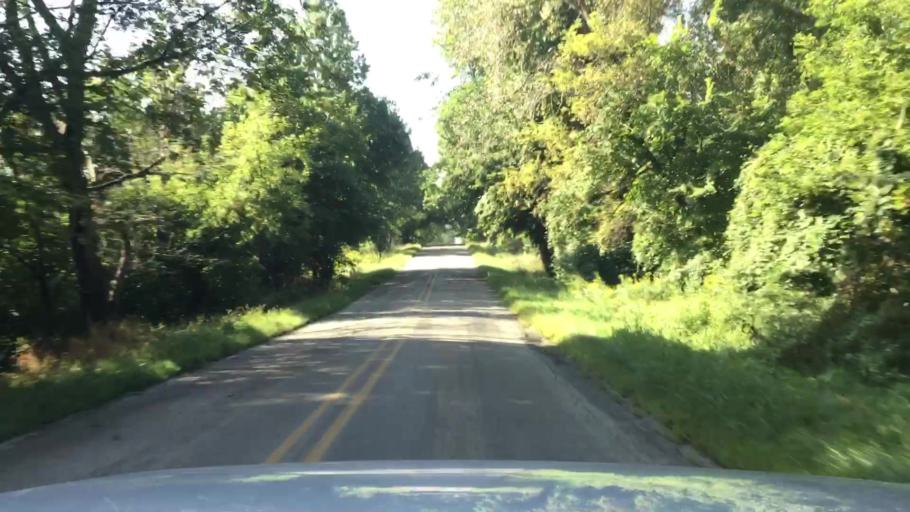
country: US
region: Michigan
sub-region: Lenawee County
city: Hudson
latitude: 41.9107
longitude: -84.4204
